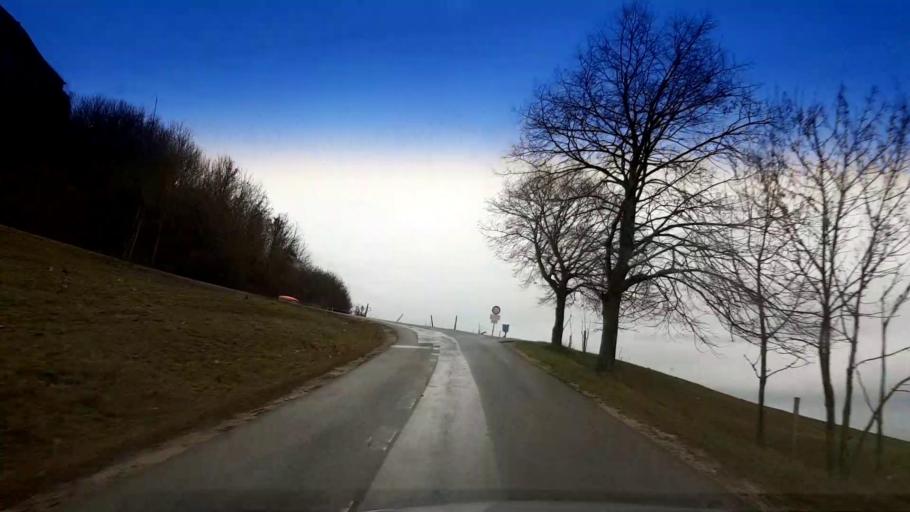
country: DE
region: Bavaria
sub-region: Upper Franconia
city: Schesslitz
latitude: 49.9561
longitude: 11.0485
